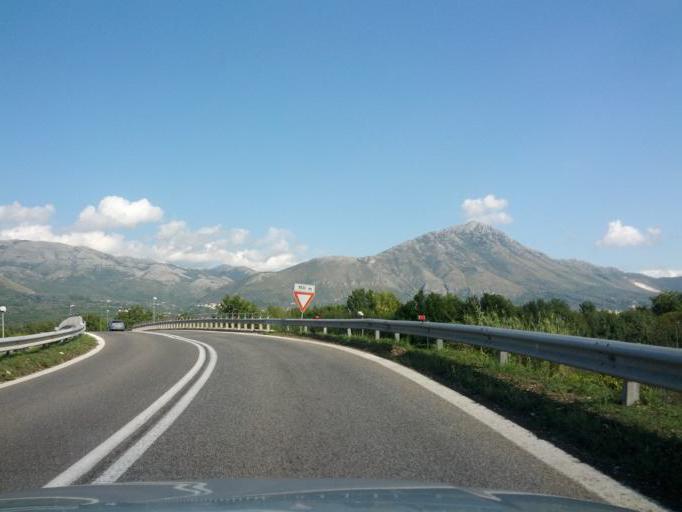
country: IT
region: Campania
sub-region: Provincia di Caserta
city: Bivio Mortola
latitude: 41.4321
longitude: 13.8977
